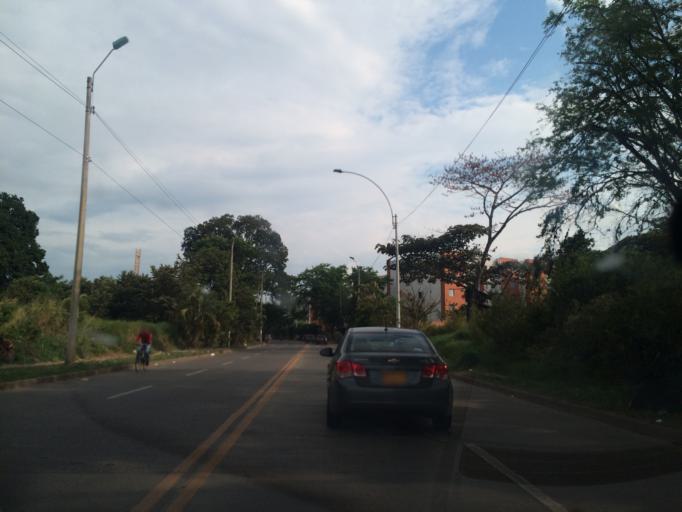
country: CO
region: Valle del Cauca
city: Cali
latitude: 3.3972
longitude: -76.5571
